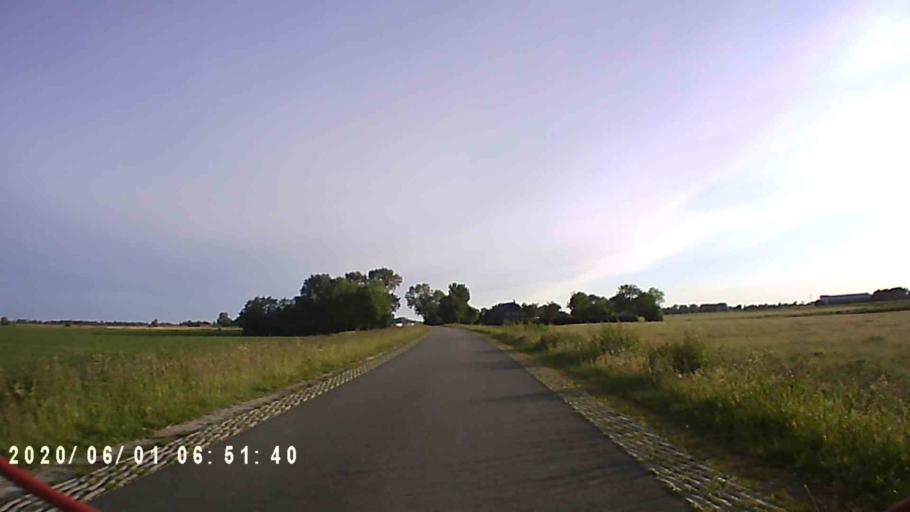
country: NL
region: Friesland
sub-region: Gemeente Kollumerland en Nieuwkruisland
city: Kollum
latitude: 53.3060
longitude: 6.1316
